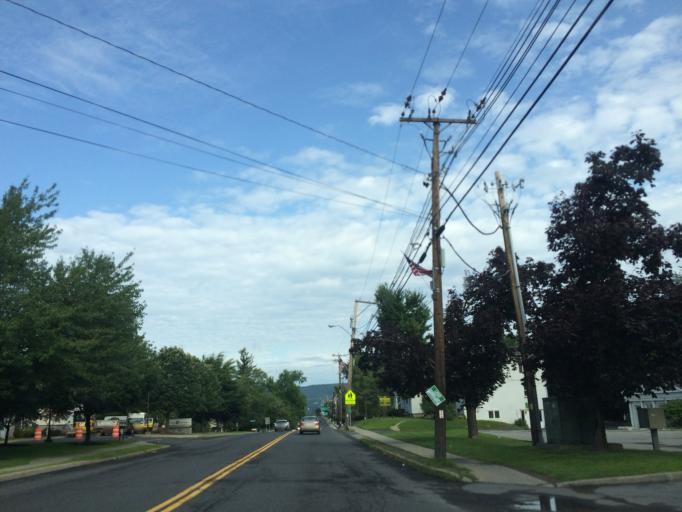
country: US
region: New York
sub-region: Ulster County
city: New Paltz
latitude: 41.7442
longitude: -74.0737
